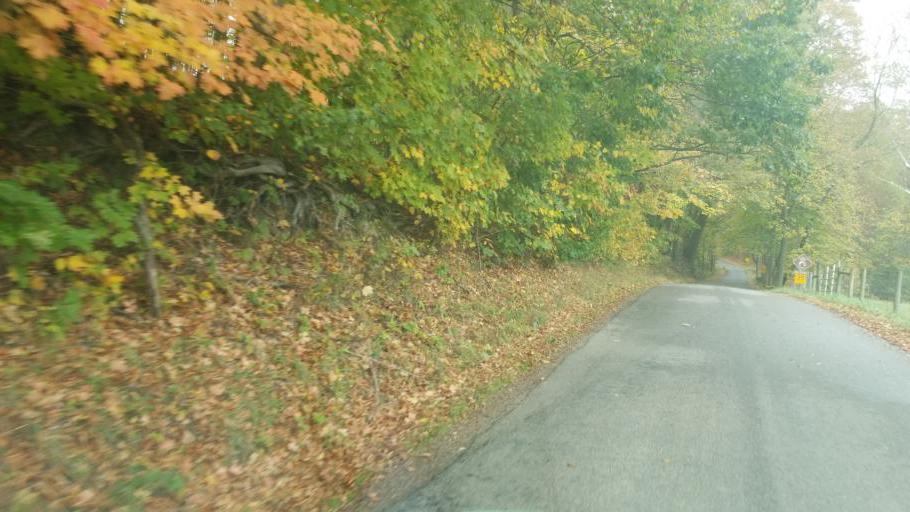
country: US
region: Ohio
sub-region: Holmes County
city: Millersburg
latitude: 40.5723
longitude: -81.8688
